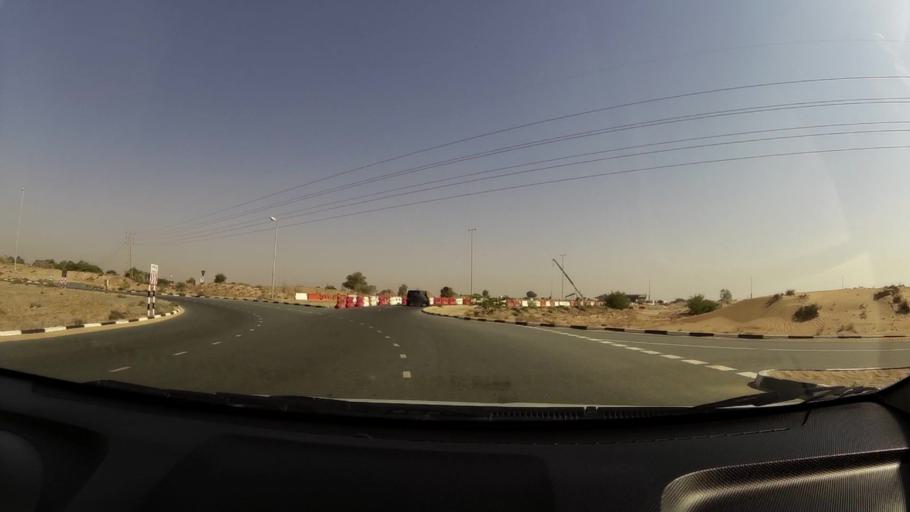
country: AE
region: Umm al Qaywayn
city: Umm al Qaywayn
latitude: 25.4714
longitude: 55.5889
